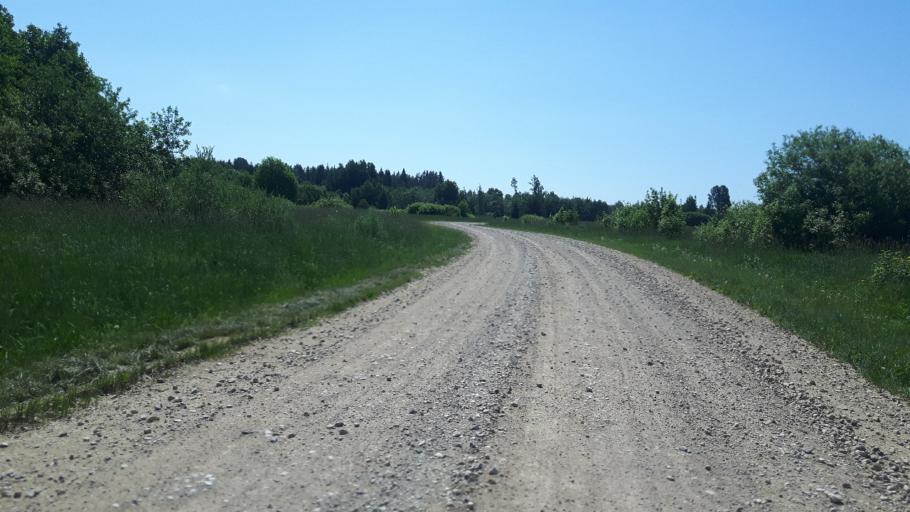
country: EE
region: Paernumaa
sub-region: Vaendra vald (alev)
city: Vandra
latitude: 58.5555
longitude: 24.9507
